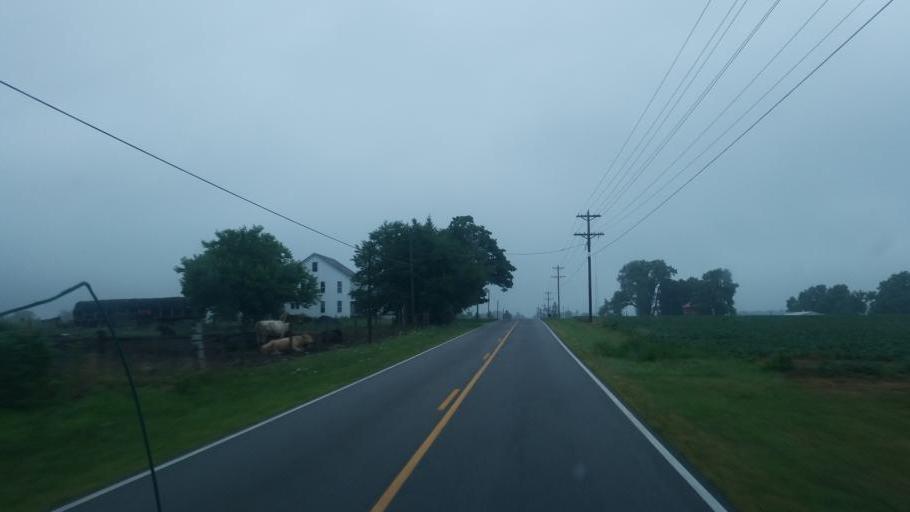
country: US
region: Ohio
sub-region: Defiance County
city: Hicksville
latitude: 41.3483
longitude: -84.7094
